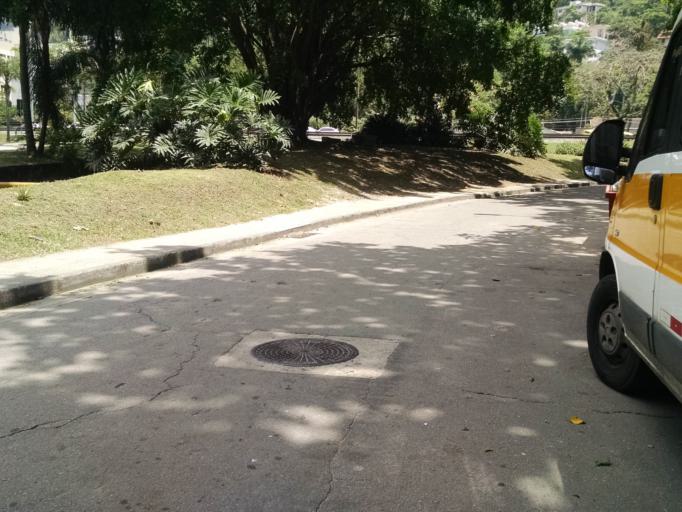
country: BR
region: Rio de Janeiro
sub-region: Rio De Janeiro
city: Rio de Janeiro
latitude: -22.9960
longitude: -43.2583
